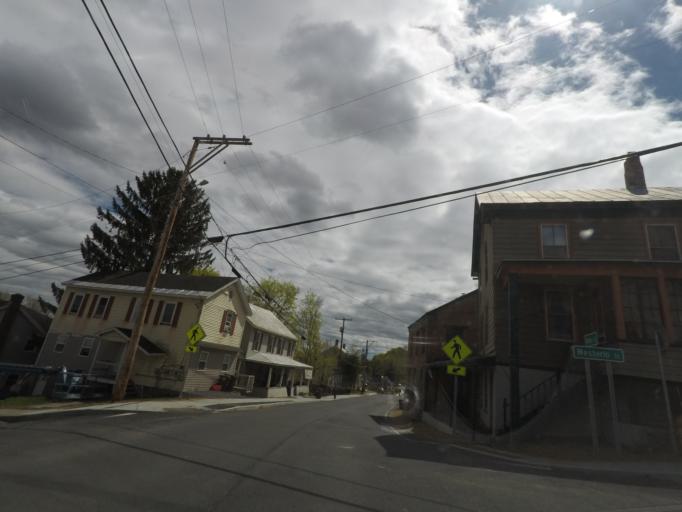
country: US
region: New York
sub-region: Albany County
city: Ravena
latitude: 42.4733
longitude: -73.7924
